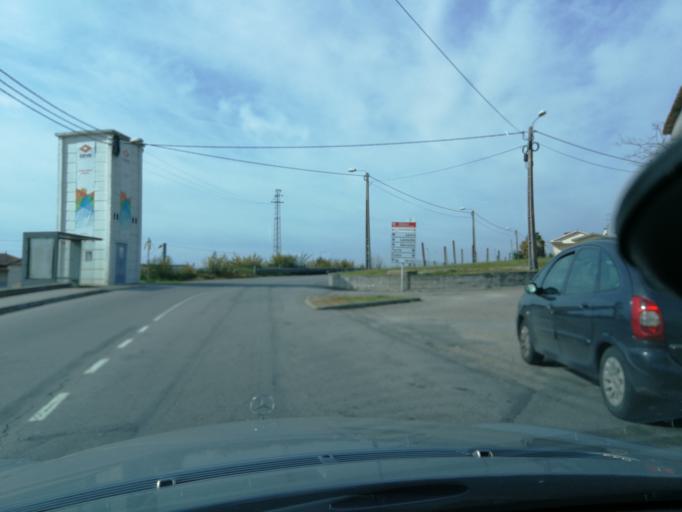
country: PT
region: Braga
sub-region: Vila Nova de Famalicao
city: Vila Nova de Famalicao
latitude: 41.4283
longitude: -8.5211
